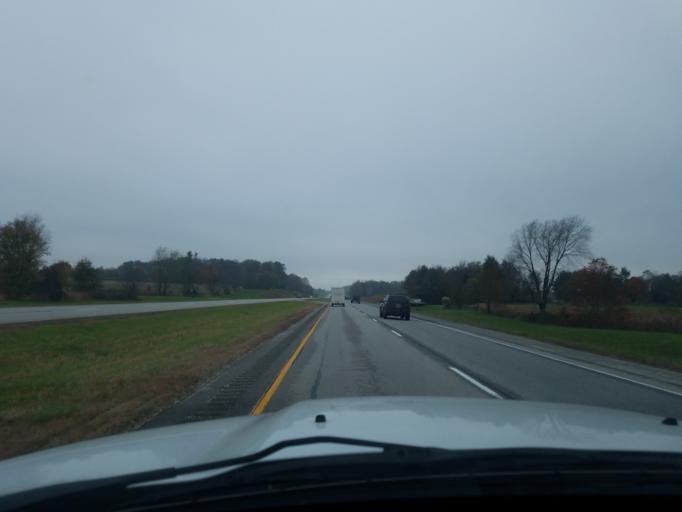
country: US
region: Kentucky
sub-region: Larue County
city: Hodgenville
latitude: 37.6172
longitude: -85.8077
